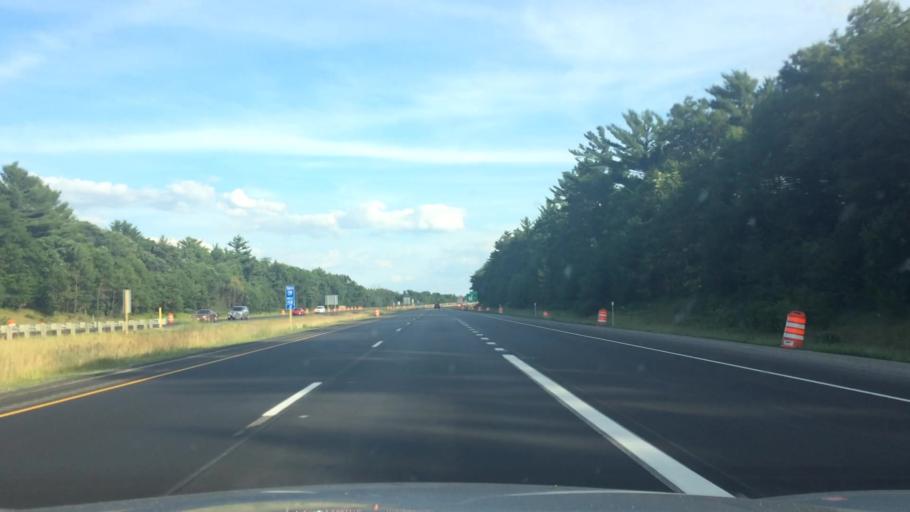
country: US
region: Wisconsin
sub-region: Portage County
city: Whiting
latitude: 44.5203
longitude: -89.5247
